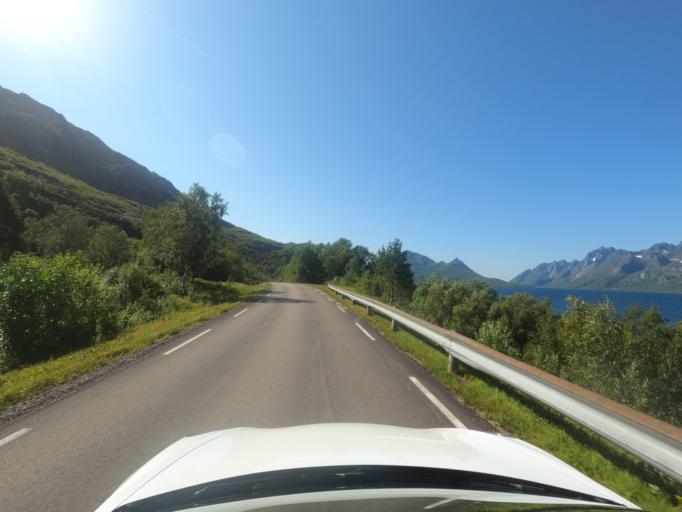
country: NO
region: Nordland
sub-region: Hadsel
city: Stokmarknes
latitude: 68.3302
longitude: 15.0162
